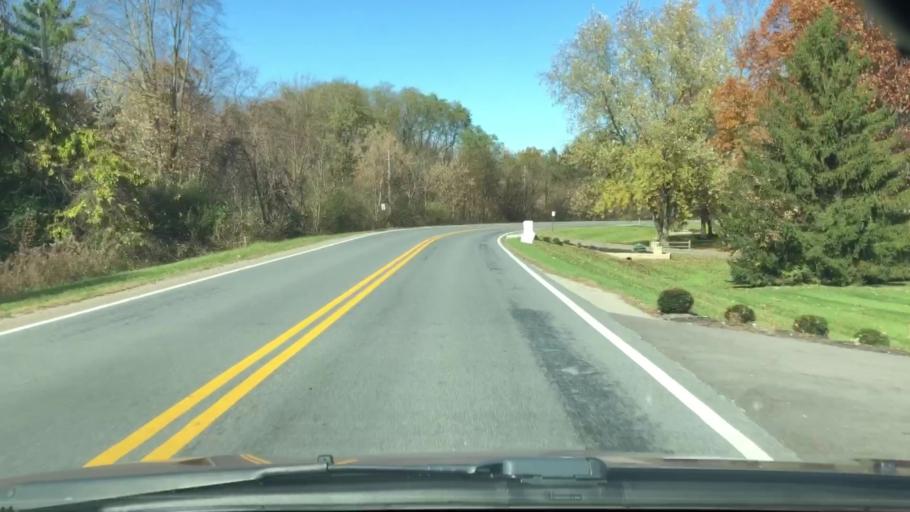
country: US
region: Ohio
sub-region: Franklin County
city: Westerville
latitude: 40.1679
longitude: -82.8800
